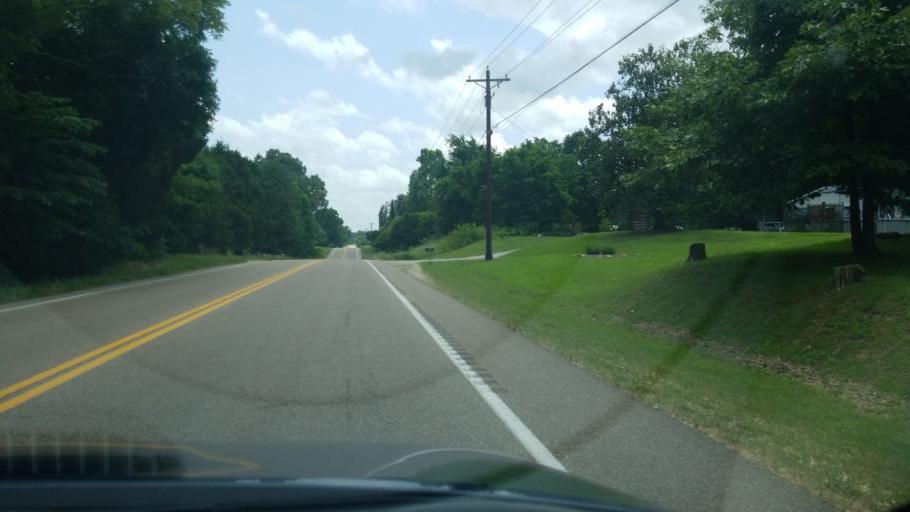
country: US
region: Tennessee
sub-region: Gibson County
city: Medina
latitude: 35.7253
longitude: -88.7165
